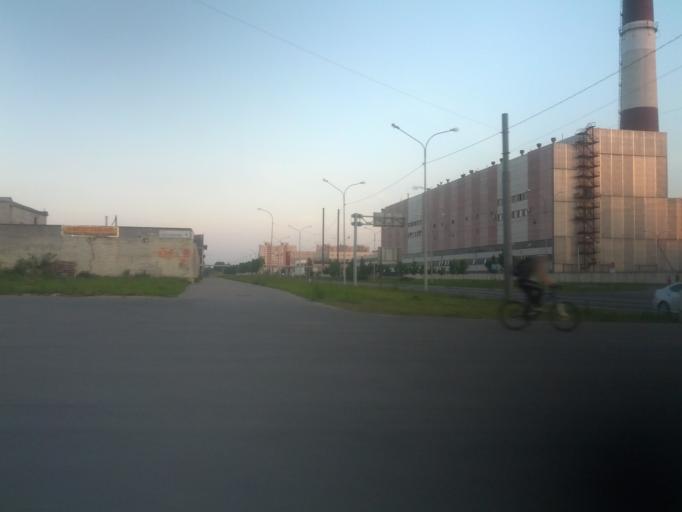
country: RU
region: St.-Petersburg
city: Staraya Derevnya
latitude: 59.9965
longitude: 30.2446
